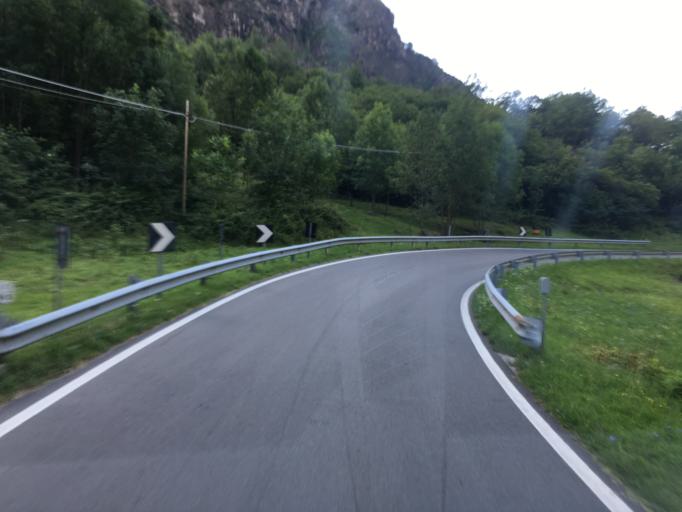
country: IT
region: Lombardy
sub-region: Provincia di Sondrio
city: San Giacomo Filippo
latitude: 46.3584
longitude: 9.3644
